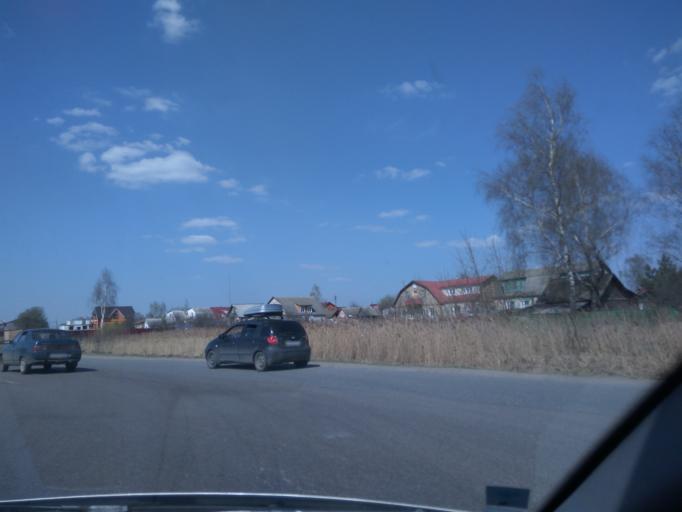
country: RU
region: Moskovskaya
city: Ramenskoye
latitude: 55.5477
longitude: 38.2837
